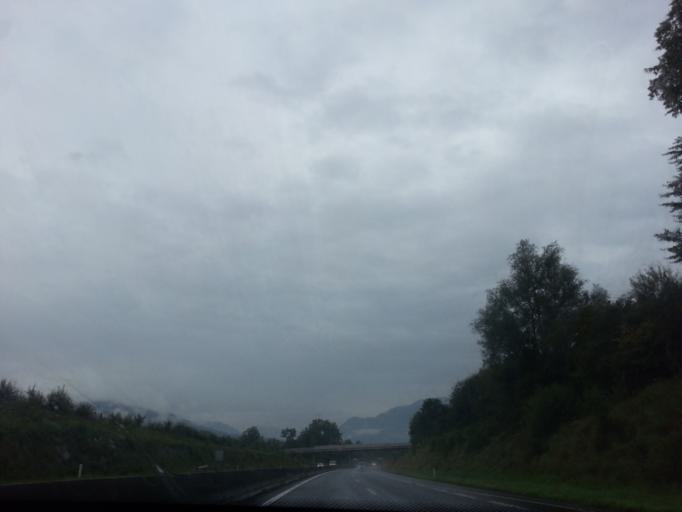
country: AT
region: Upper Austria
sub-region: Politischer Bezirk Kirchdorf an der Krems
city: Micheldorf in Oberoesterreich
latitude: 47.9551
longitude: 14.1012
